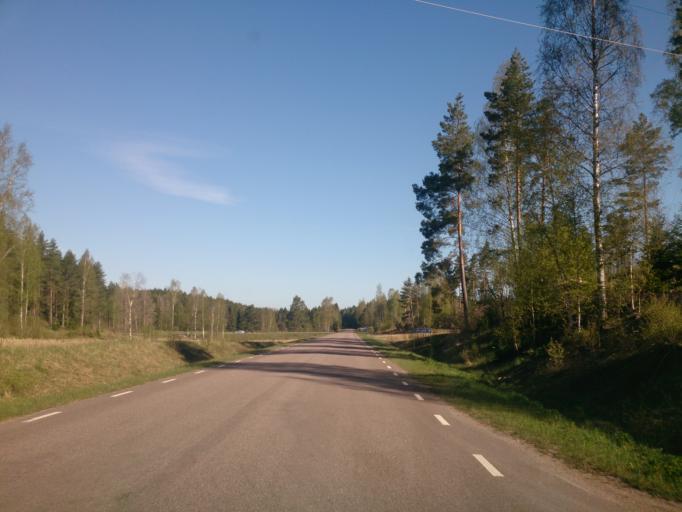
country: SE
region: OEstergoetland
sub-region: Linkopings Kommun
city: Ljungsbro
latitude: 58.5882
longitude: 15.5041
